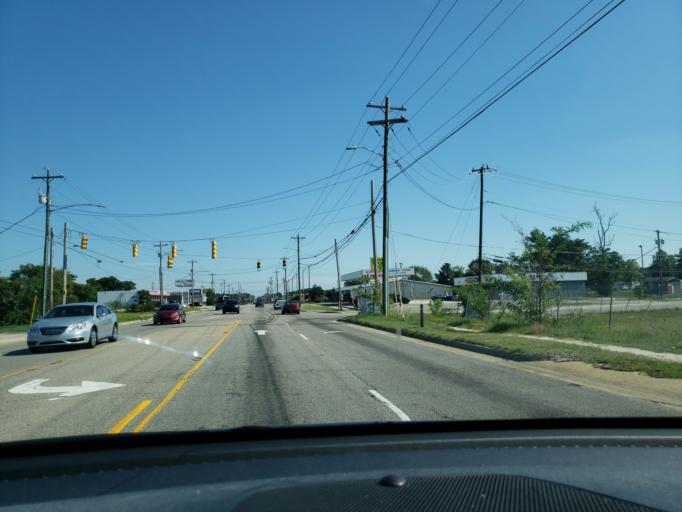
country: US
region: North Carolina
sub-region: Cumberland County
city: Spring Lake
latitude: 35.1150
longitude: -78.9307
